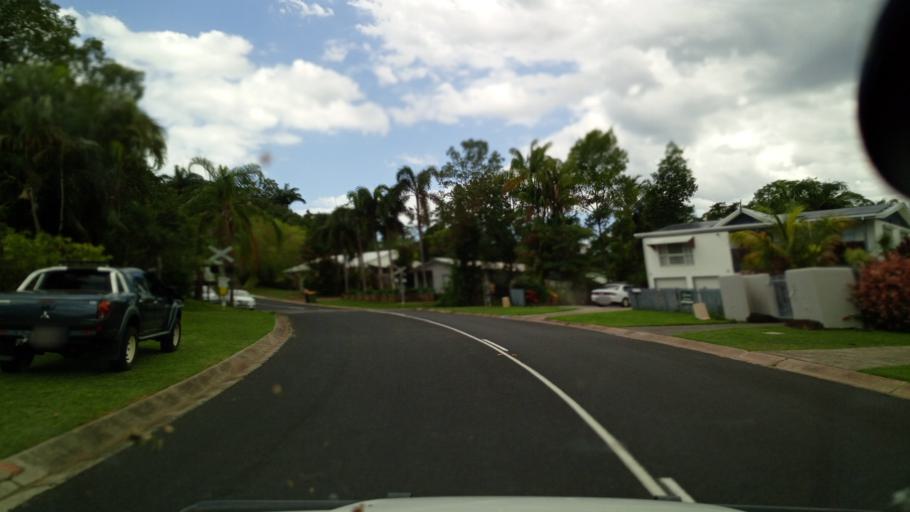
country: AU
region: Queensland
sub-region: Cairns
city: Redlynch
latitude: -16.9072
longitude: 145.7160
